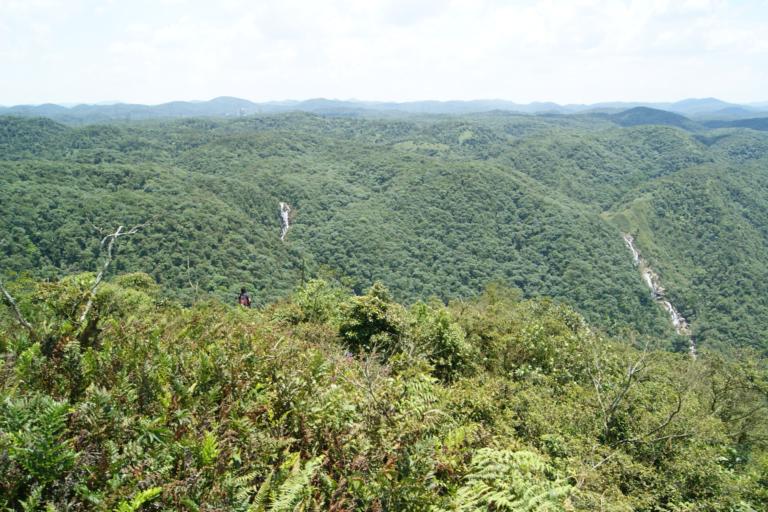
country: BR
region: Sao Paulo
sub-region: Rio Grande Da Serra
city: Rio Grande da Serra
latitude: -23.7952
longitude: -46.3738
